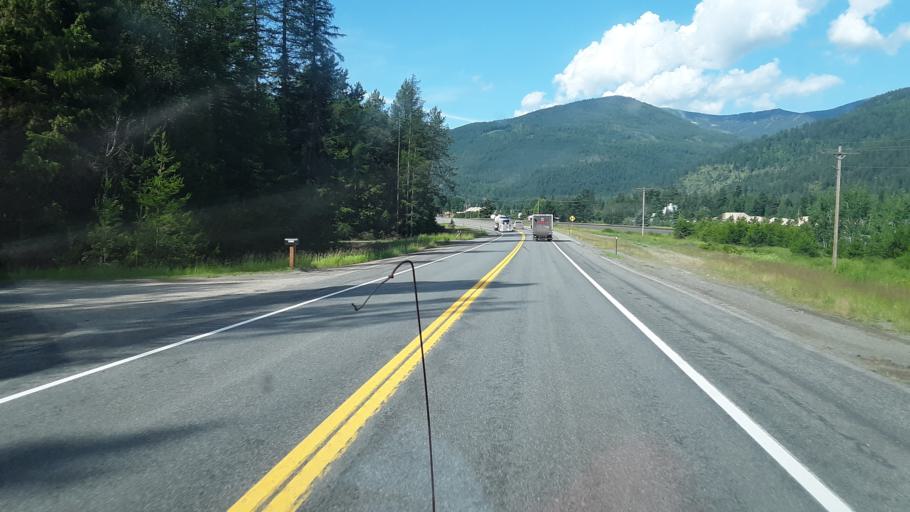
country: US
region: Idaho
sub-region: Bonner County
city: Ponderay
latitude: 48.4105
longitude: -116.5217
